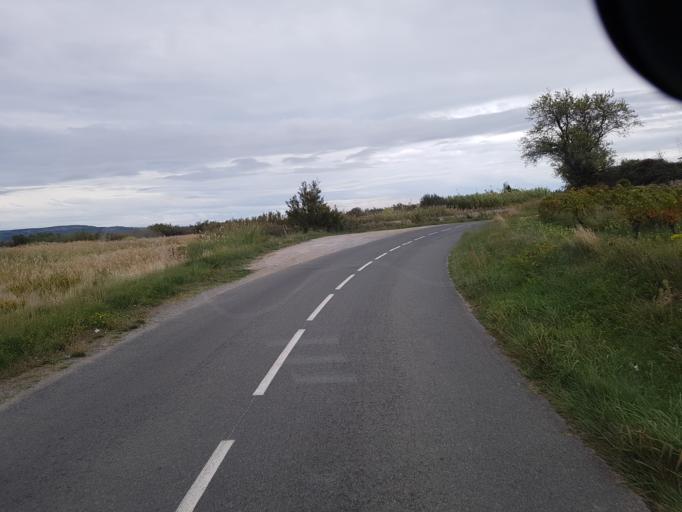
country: FR
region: Languedoc-Roussillon
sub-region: Departement de l'Aude
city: Narbonne
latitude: 43.1379
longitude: 2.9804
